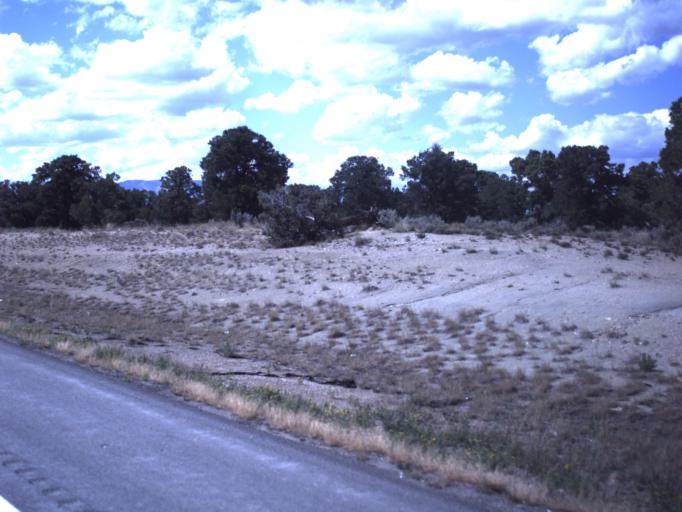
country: US
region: Utah
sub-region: Duchesne County
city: Duchesne
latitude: 40.1867
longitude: -110.6709
